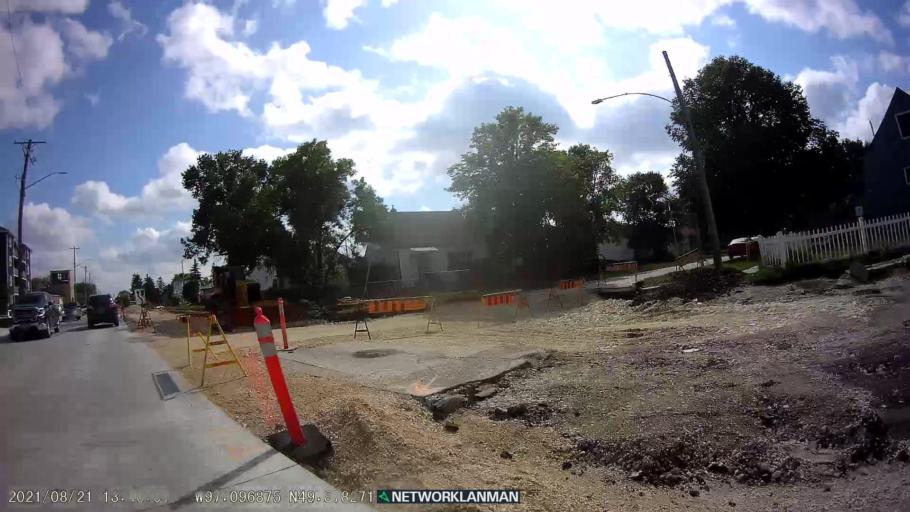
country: CA
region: Manitoba
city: Winnipeg
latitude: 49.8781
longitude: -97.0968
